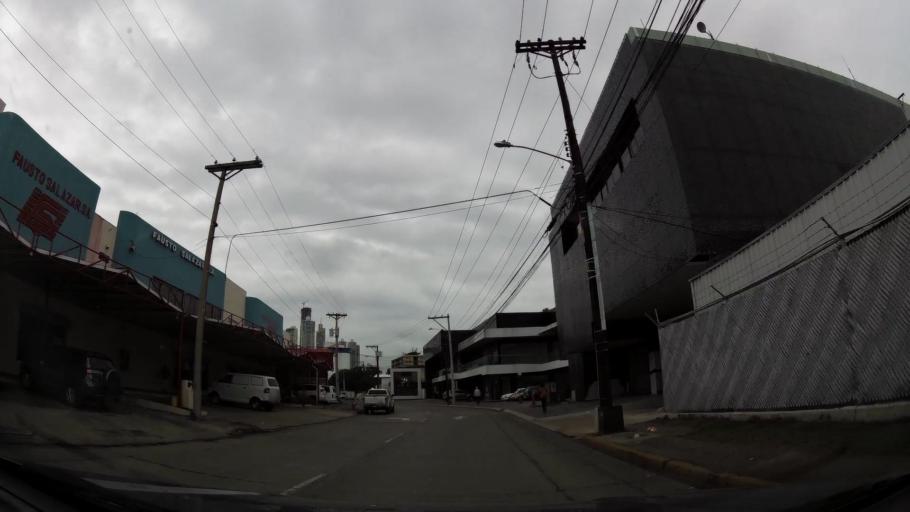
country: PA
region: Panama
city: Panama
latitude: 9.0027
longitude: -79.5248
